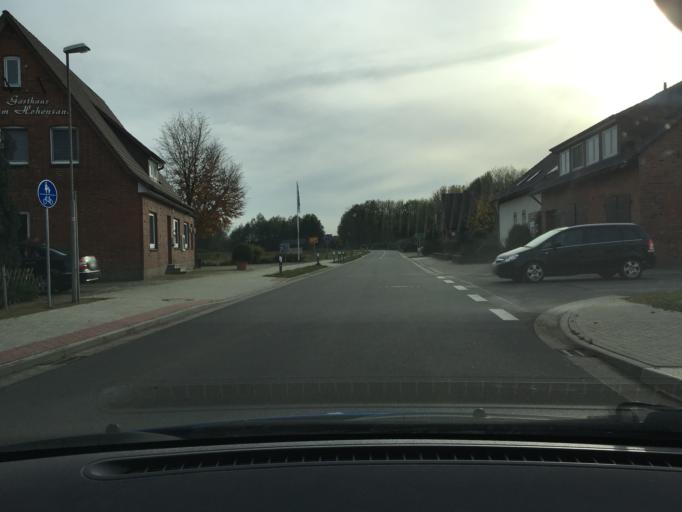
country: DE
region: Lower Saxony
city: Bardowick
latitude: 53.3124
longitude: 10.3866
